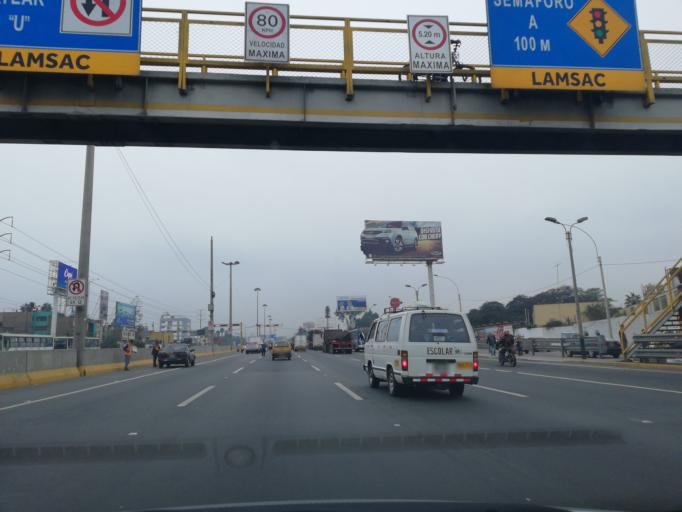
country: PE
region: Lima
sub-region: Lima
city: San Luis
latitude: -12.0741
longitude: -76.9742
